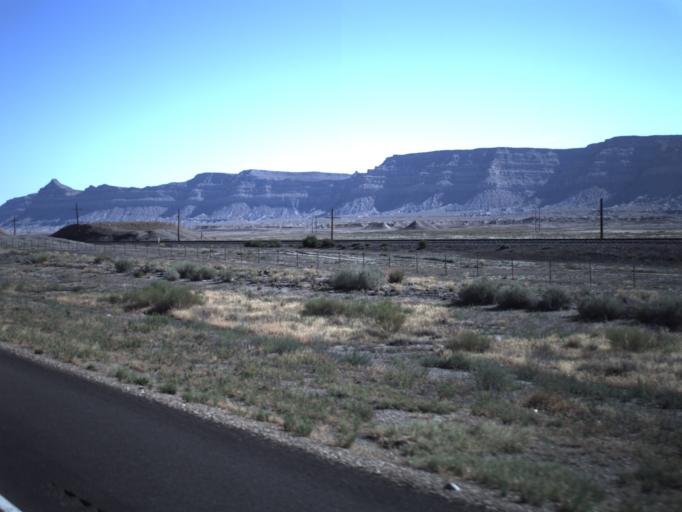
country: US
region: Utah
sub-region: Carbon County
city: East Carbon City
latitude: 39.0828
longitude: -110.3184
